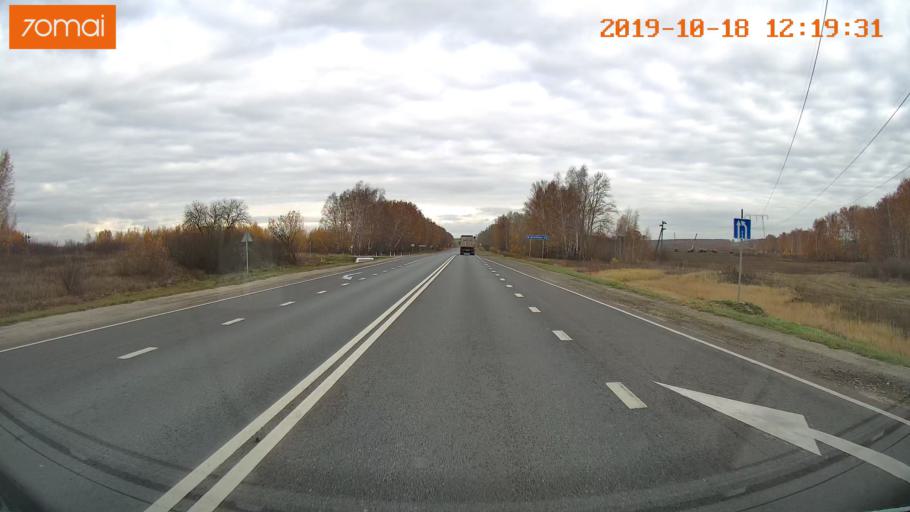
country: RU
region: Rjazan
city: Zakharovo
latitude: 54.4835
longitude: 39.4690
